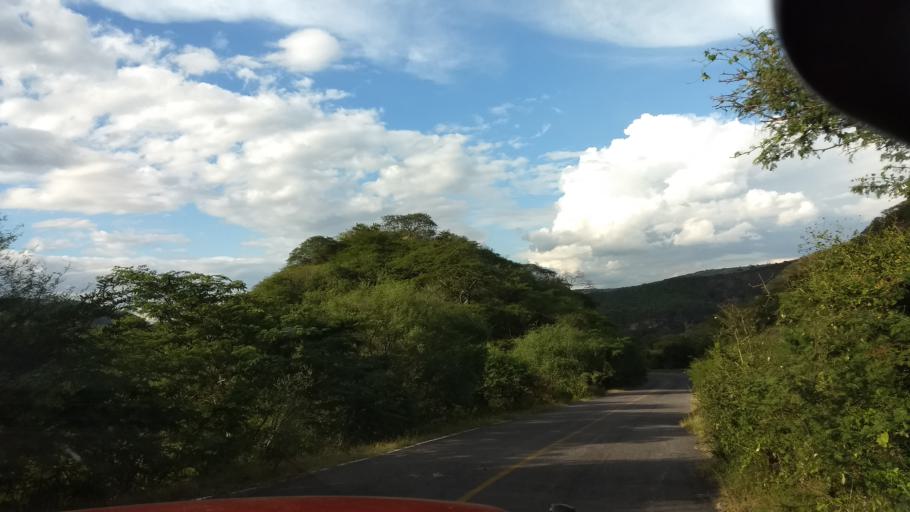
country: MX
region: Colima
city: Suchitlan
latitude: 19.4535
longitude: -103.8214
